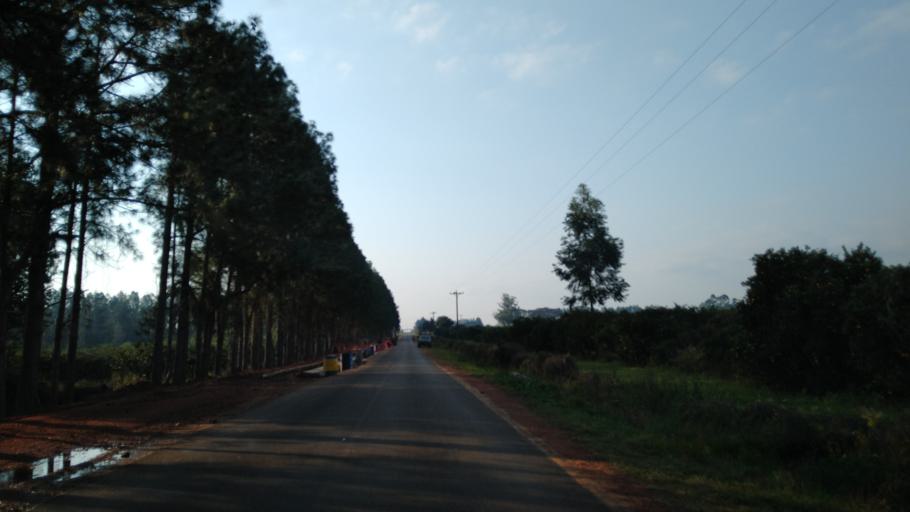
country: AR
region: Entre Rios
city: Santa Ana
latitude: -30.9077
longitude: -57.9257
